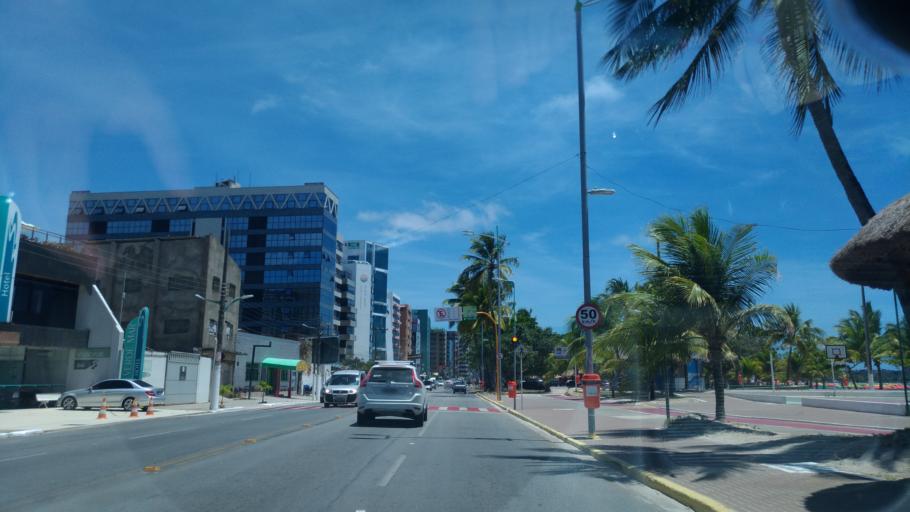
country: BR
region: Alagoas
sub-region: Maceio
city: Maceio
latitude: -9.6738
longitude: -35.7171
